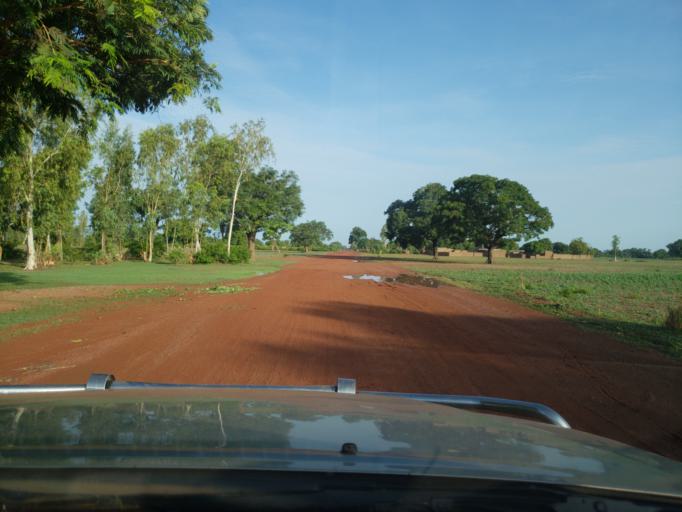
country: ML
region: Sikasso
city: Koutiala
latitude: 12.4168
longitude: -5.5720
